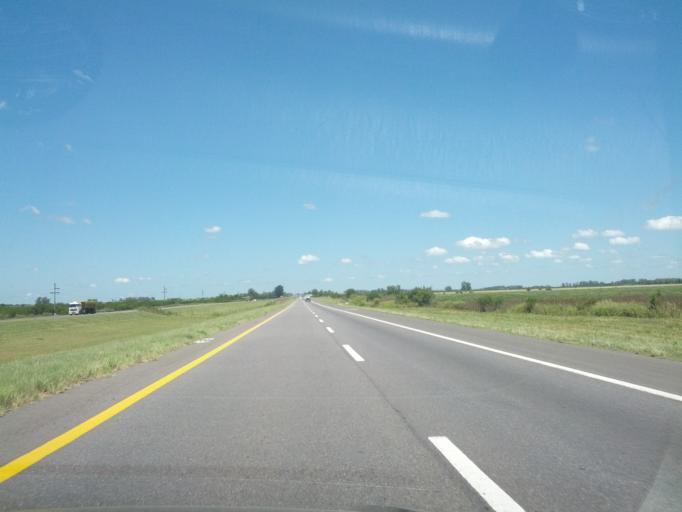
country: AR
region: Entre Rios
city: Gualeguaychu
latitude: -33.1375
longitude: -58.6594
